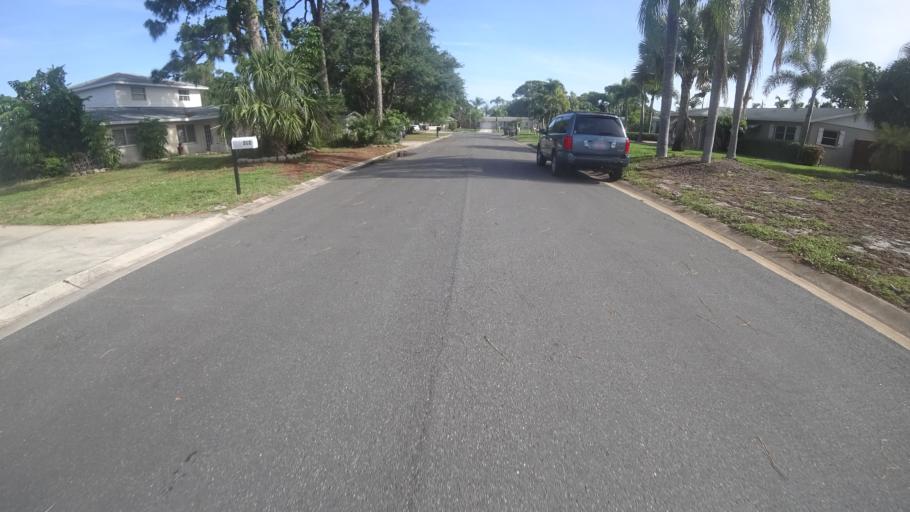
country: US
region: Florida
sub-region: Manatee County
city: West Bradenton
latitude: 27.5020
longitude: -82.6234
